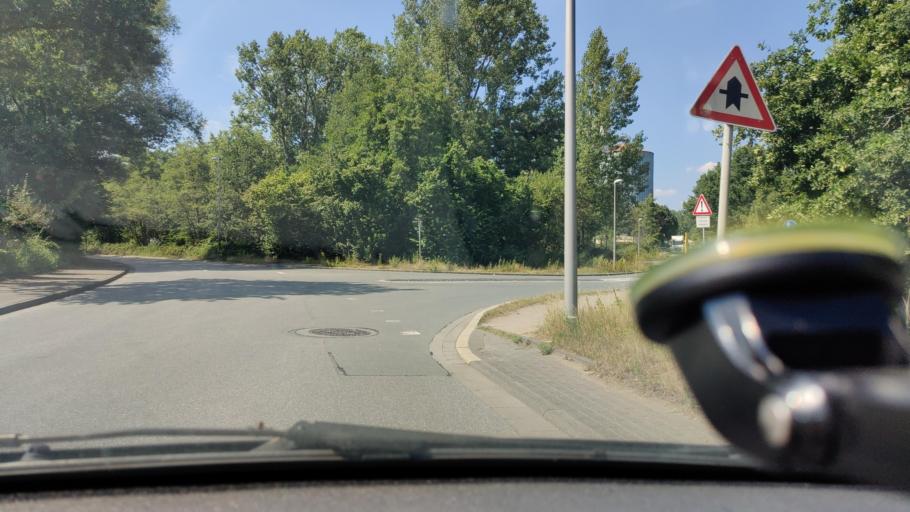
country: DE
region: North Rhine-Westphalia
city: Dorsten
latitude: 51.6594
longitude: 7.0194
